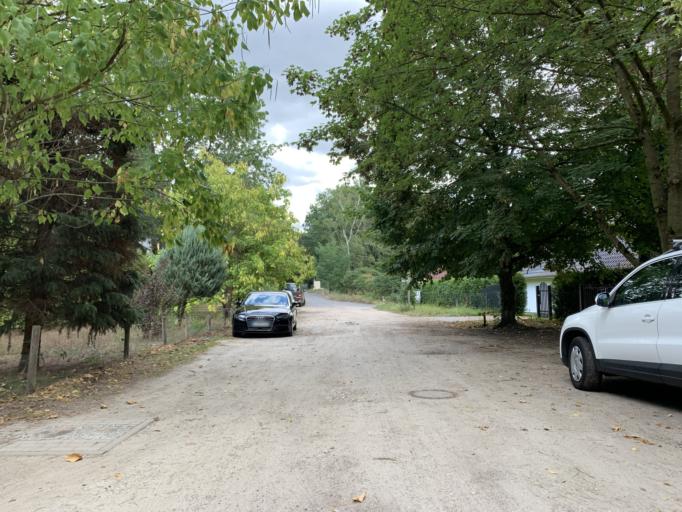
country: DE
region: Berlin
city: Wannsee
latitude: 52.4014
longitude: 13.1770
